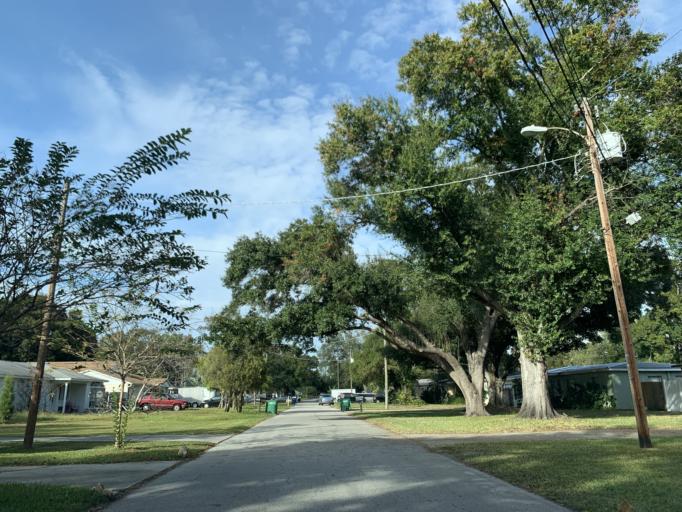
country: US
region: Florida
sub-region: Hillsborough County
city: Tampa
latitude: 27.9018
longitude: -82.5106
